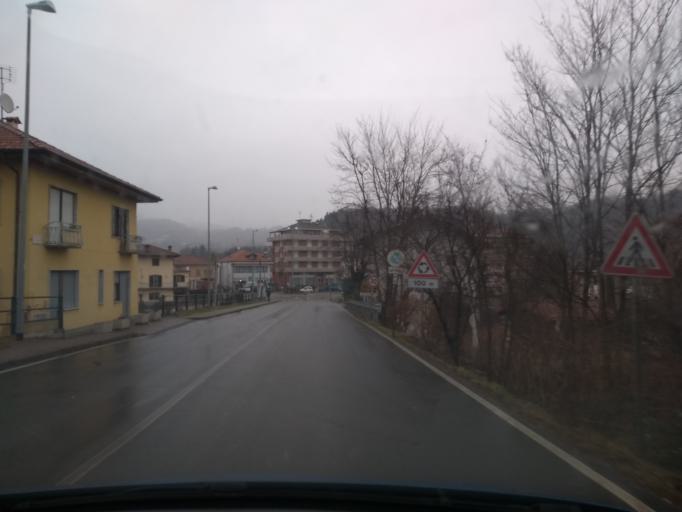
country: IT
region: Piedmont
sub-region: Provincia di Torino
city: Cuorgne
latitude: 45.3954
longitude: 7.6546
